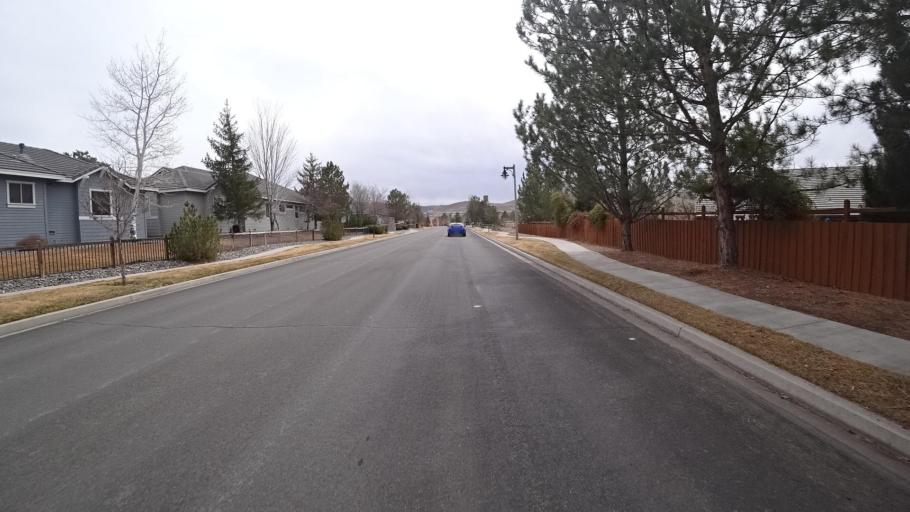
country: US
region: Nevada
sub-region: Washoe County
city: Spanish Springs
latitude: 39.6134
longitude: -119.6912
